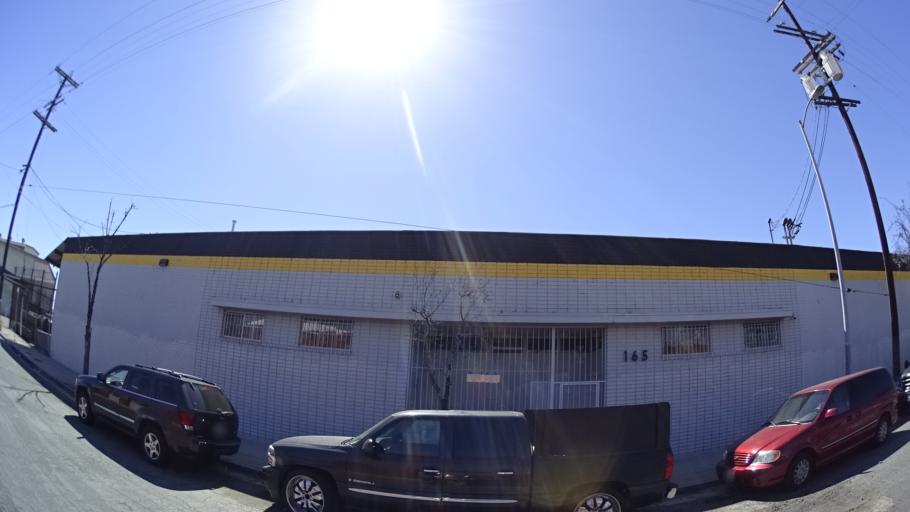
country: US
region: California
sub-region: Los Angeles County
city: Los Angeles
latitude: 34.0460
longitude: -118.2280
